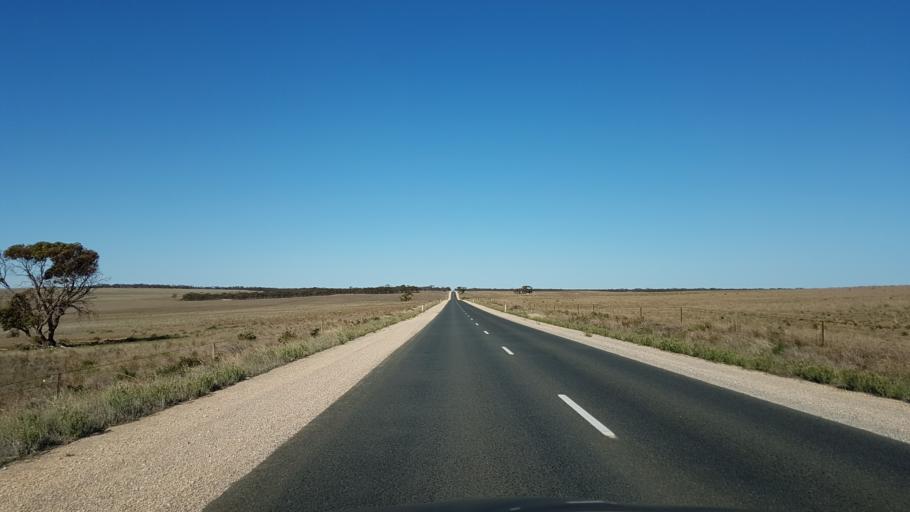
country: AU
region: South Australia
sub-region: Mid Murray
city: Mannum
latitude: -34.7562
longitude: 139.4596
